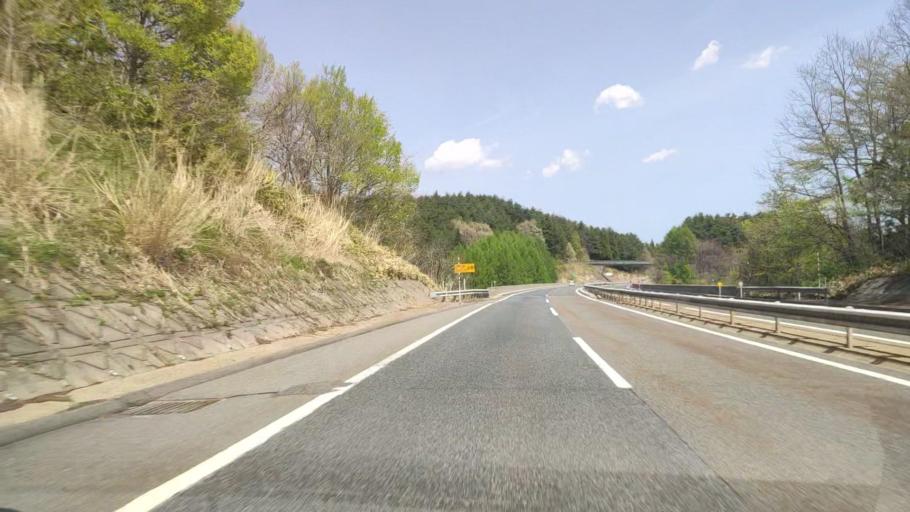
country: JP
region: Iwate
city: Ichinohe
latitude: 40.2720
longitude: 141.3993
